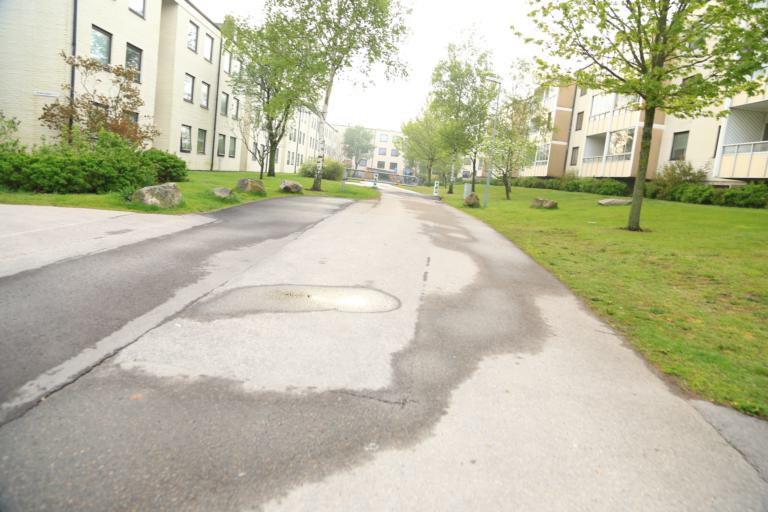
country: SE
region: Halland
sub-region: Varbergs Kommun
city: Varberg
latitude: 57.0939
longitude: 12.2675
